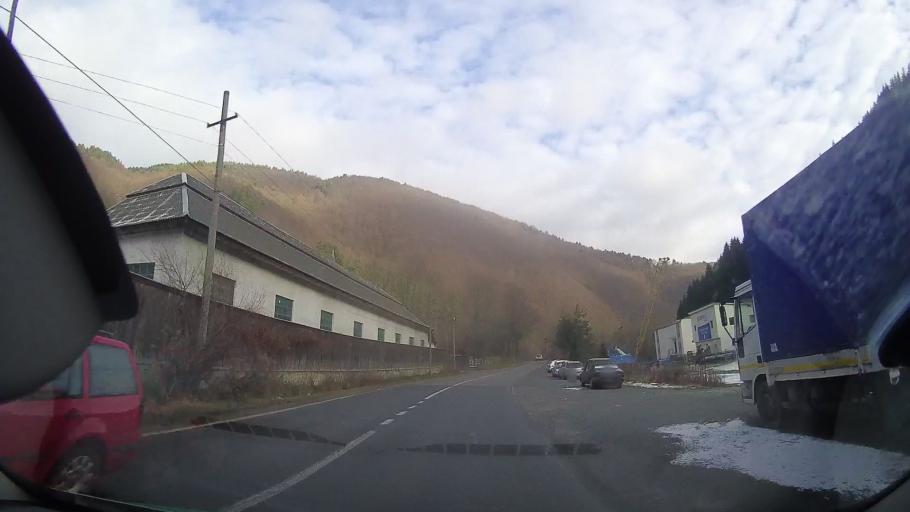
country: RO
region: Alba
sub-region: Comuna Lupsa
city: Lupsa
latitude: 46.3783
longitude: 23.1529
